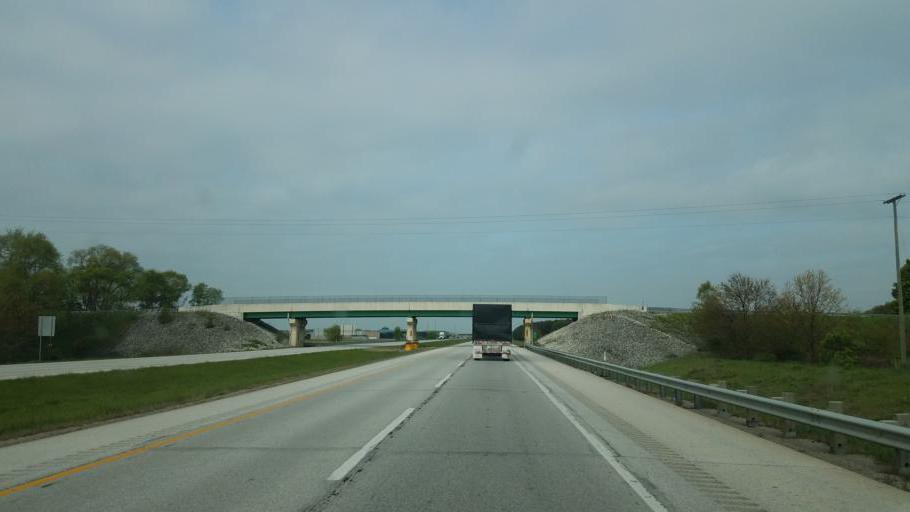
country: US
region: Indiana
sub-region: Elkhart County
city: Bristol
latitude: 41.7311
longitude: -85.8692
